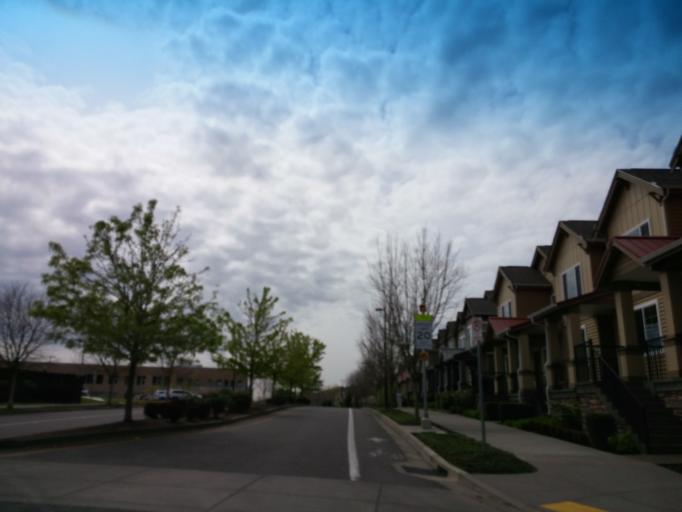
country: US
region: Oregon
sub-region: Washington County
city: Cedar Mill
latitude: 45.5258
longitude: -122.7979
